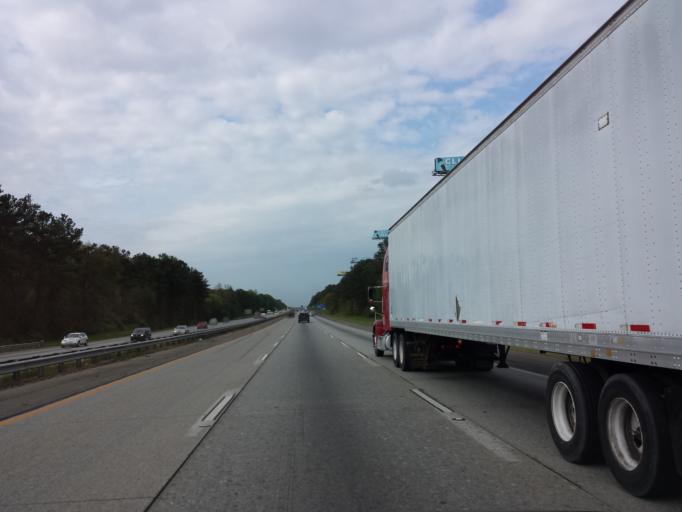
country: US
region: Georgia
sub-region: Peach County
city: Byron
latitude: 32.6295
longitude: -83.7432
